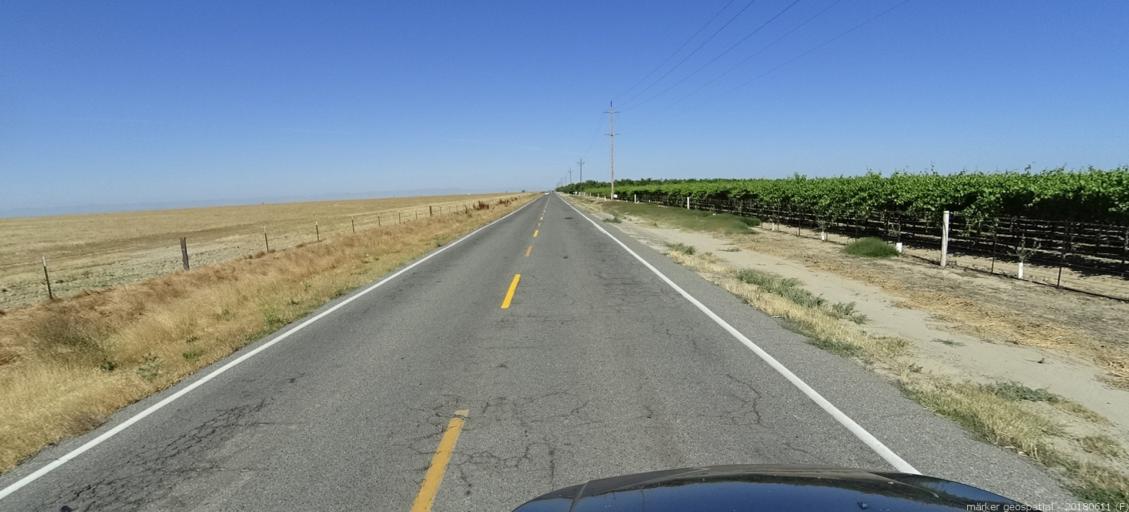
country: US
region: California
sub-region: Madera County
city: Madera
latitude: 36.9236
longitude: -120.1881
